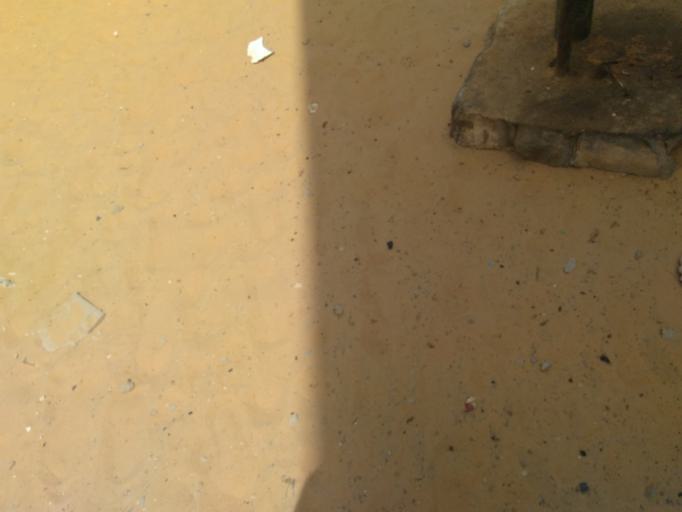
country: SN
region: Dakar
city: Pikine
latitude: 14.7992
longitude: -17.3378
